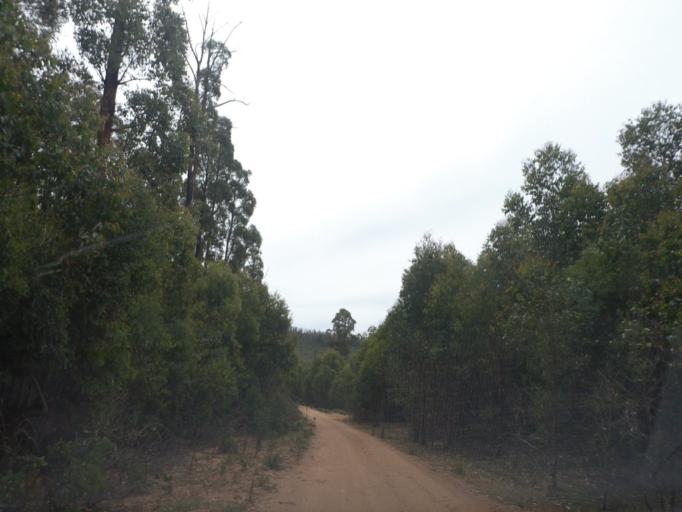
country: AU
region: Victoria
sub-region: Murrindindi
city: Alexandra
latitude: -37.3944
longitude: 145.5876
